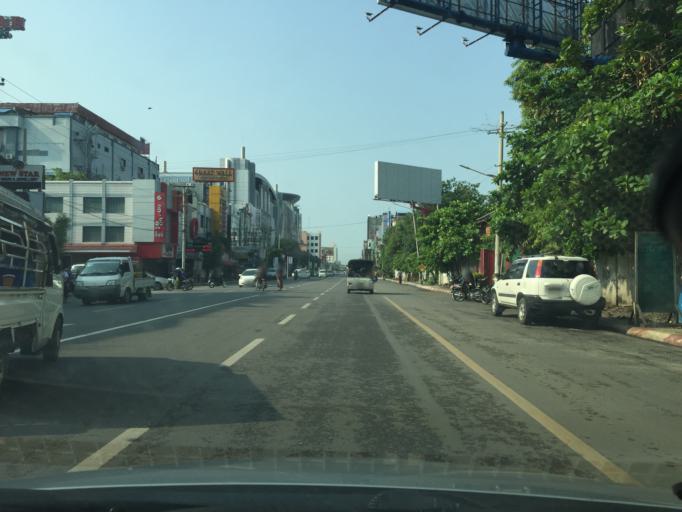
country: MM
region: Mandalay
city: Mandalay
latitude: 21.9734
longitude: 96.0866
